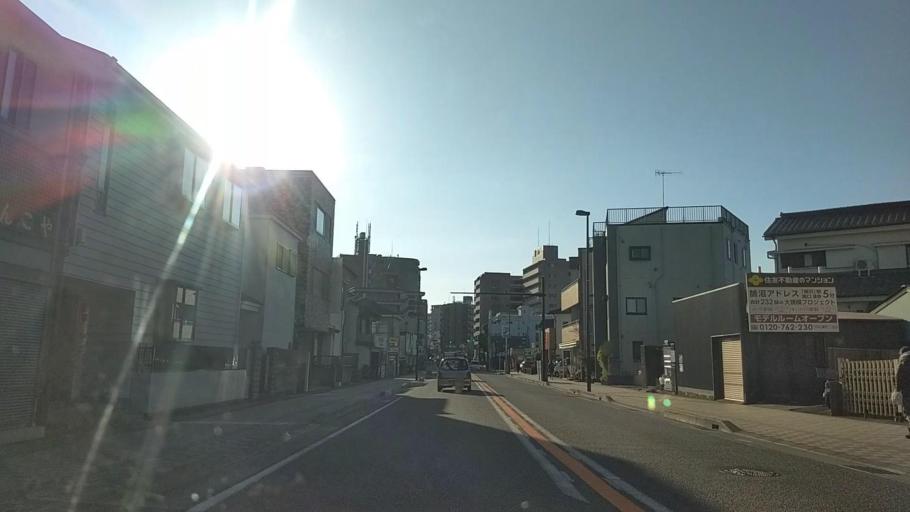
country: JP
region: Kanagawa
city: Fujisawa
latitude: 35.3445
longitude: 139.4873
